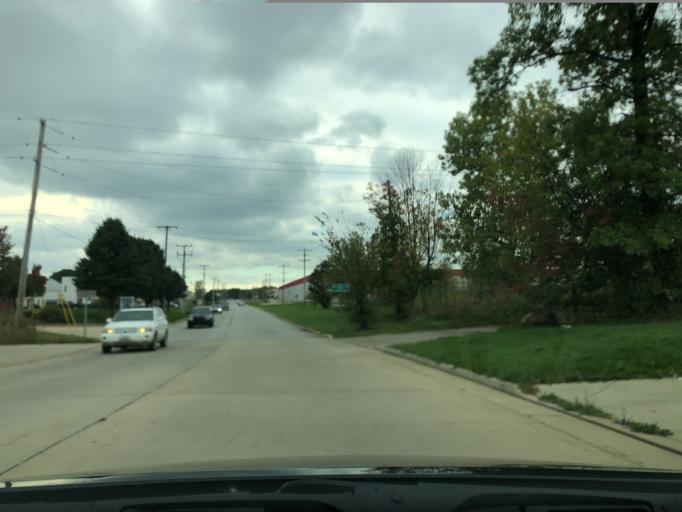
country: US
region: Ohio
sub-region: Summit County
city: Cuyahoga Falls
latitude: 41.1708
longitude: -81.4986
